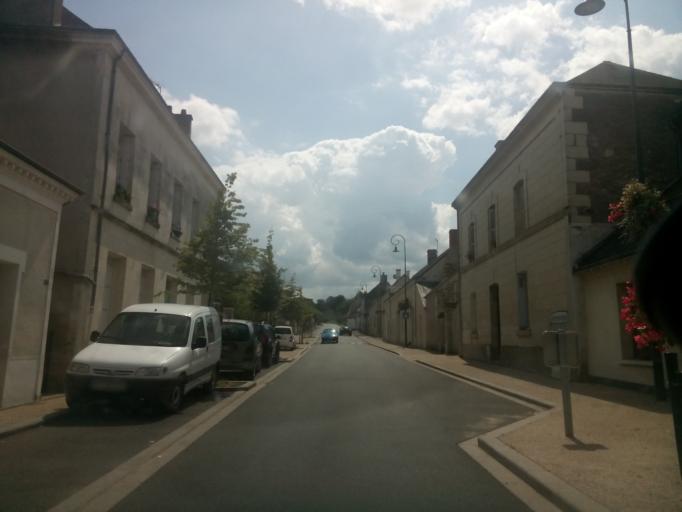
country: FR
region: Centre
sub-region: Departement d'Indre-et-Loire
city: Langeais
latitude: 47.2966
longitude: 0.4168
